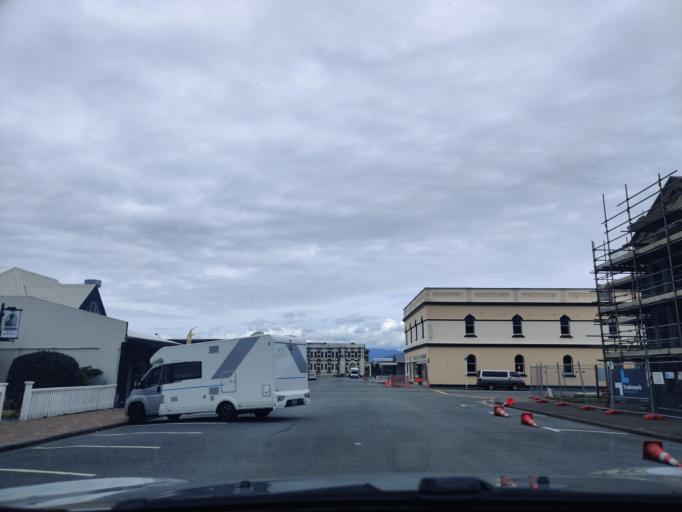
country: NZ
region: West Coast
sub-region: Westland District
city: Hokitika
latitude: -42.7183
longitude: 170.9611
